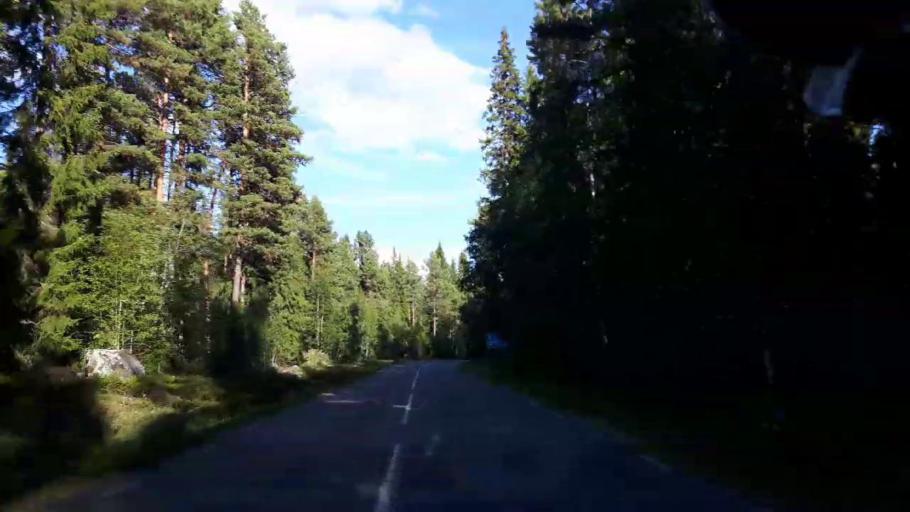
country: SE
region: Jaemtland
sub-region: Stroemsunds Kommun
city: Stroemsund
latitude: 63.3688
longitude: 15.5661
